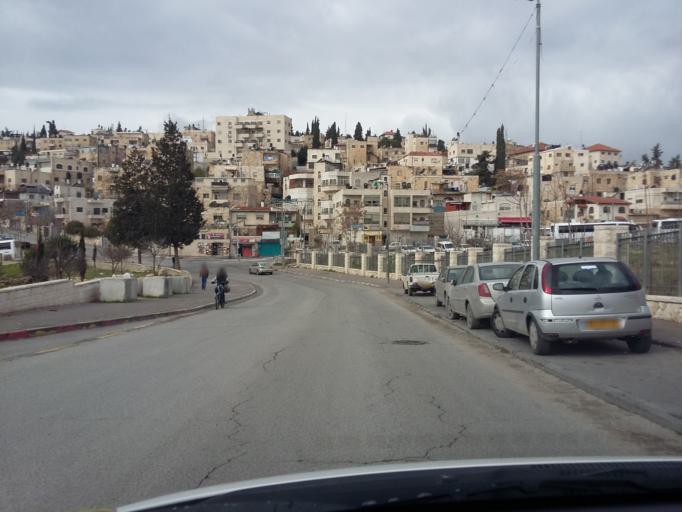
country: PS
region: West Bank
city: East Jerusalem
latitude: 31.7863
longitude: 35.2400
